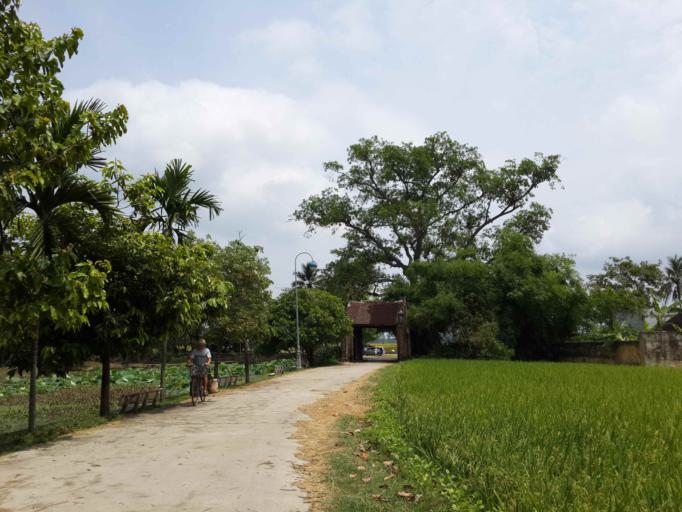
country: VN
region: Ha Noi
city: Son Tay
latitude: 21.1579
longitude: 105.4723
